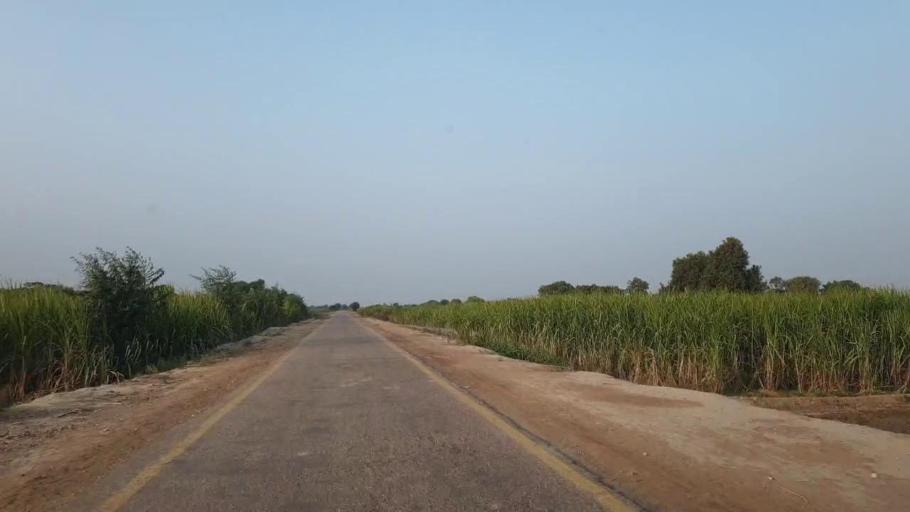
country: PK
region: Sindh
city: Tando Ghulam Ali
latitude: 25.0914
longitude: 68.9586
